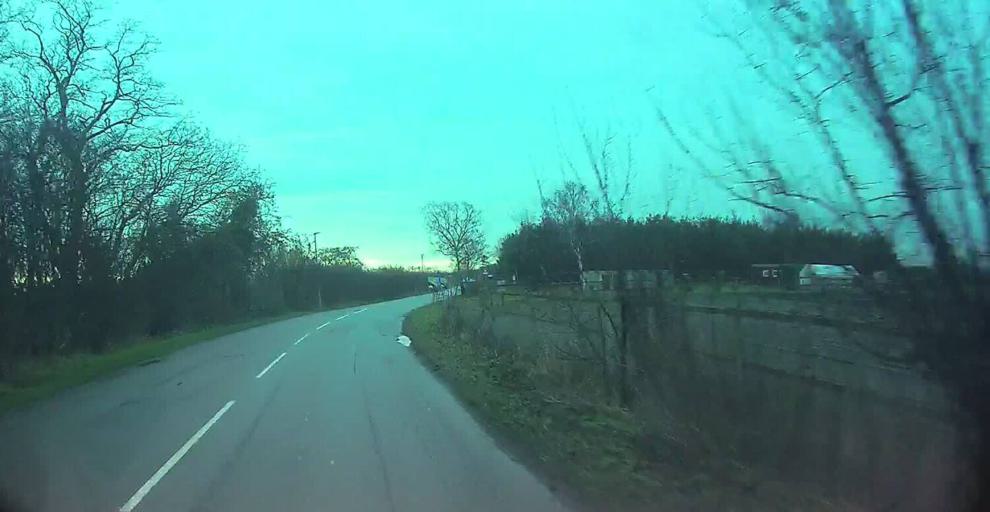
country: DK
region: Capital Region
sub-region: Tarnby Kommune
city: Tarnby
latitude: 55.5993
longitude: 12.6030
